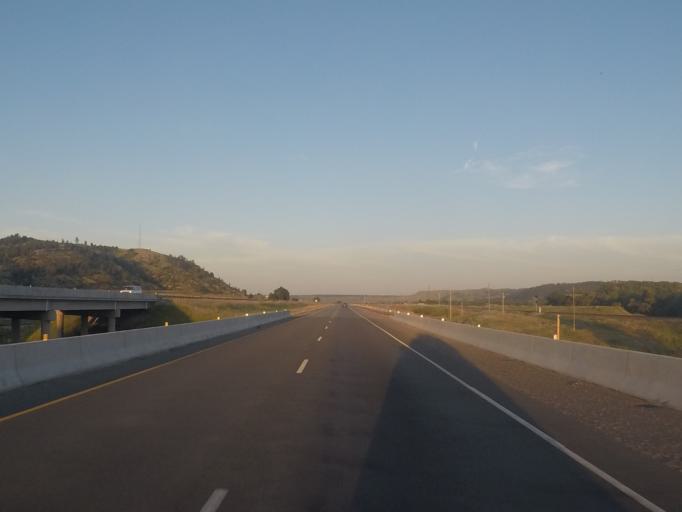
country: US
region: Montana
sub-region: Stillwater County
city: Columbus
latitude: 45.6047
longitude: -109.1584
